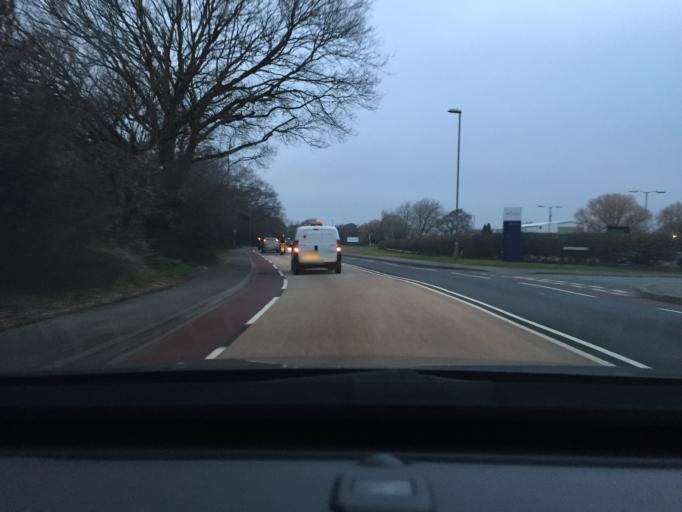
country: GB
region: England
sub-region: Hampshire
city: Fareham
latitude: 50.8296
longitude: -1.1681
